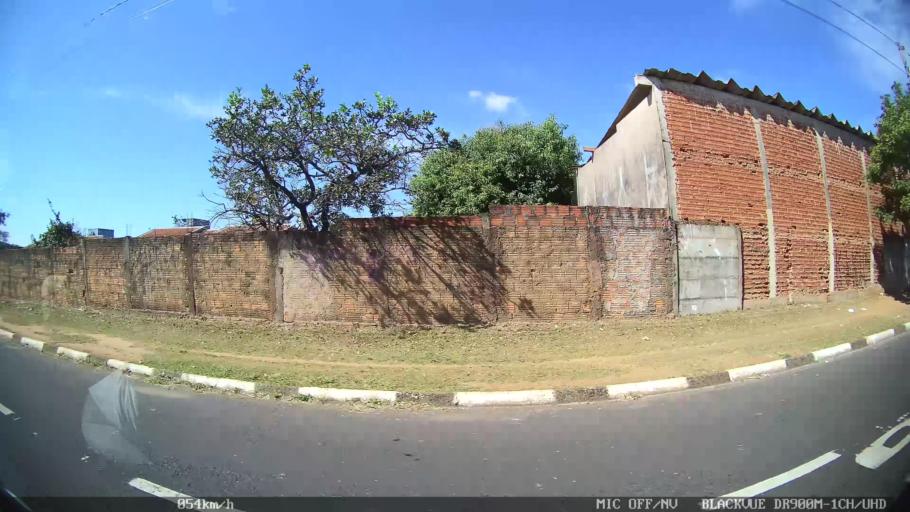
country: BR
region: Sao Paulo
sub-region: Franca
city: Franca
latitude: -20.5054
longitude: -47.3989
